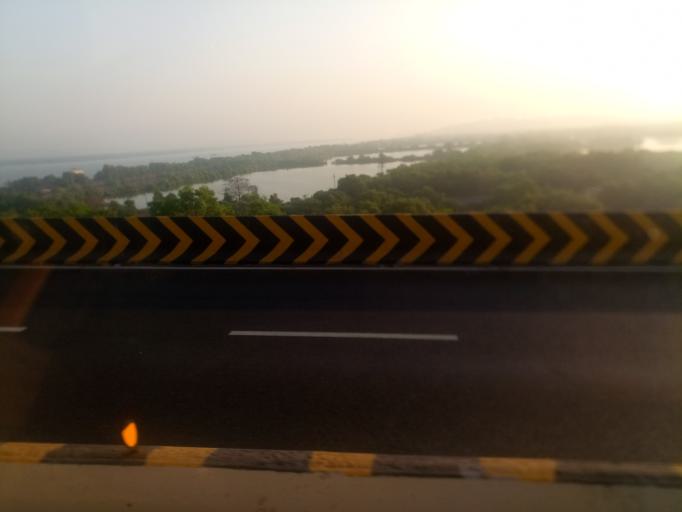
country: IN
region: Goa
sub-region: North Goa
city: Panaji
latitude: 15.4960
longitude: 73.8371
